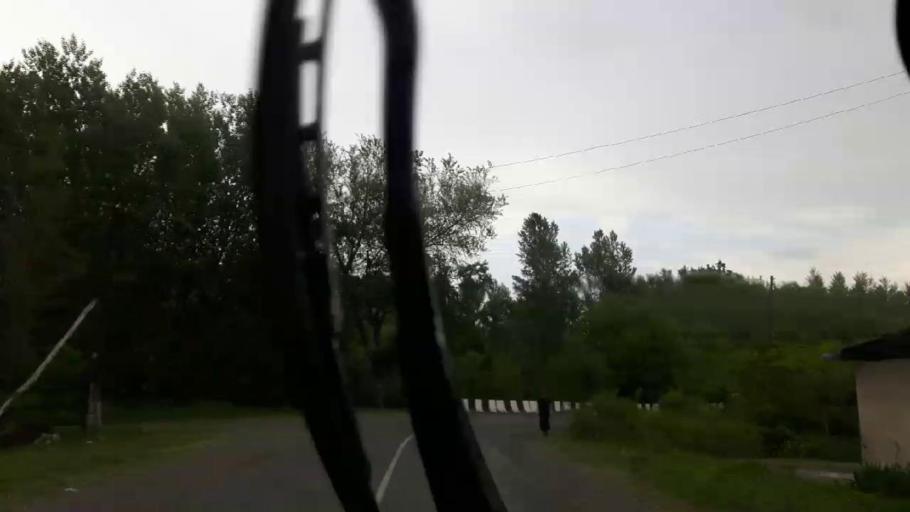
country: GE
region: Shida Kartli
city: Gori
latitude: 41.9613
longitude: 44.2163
